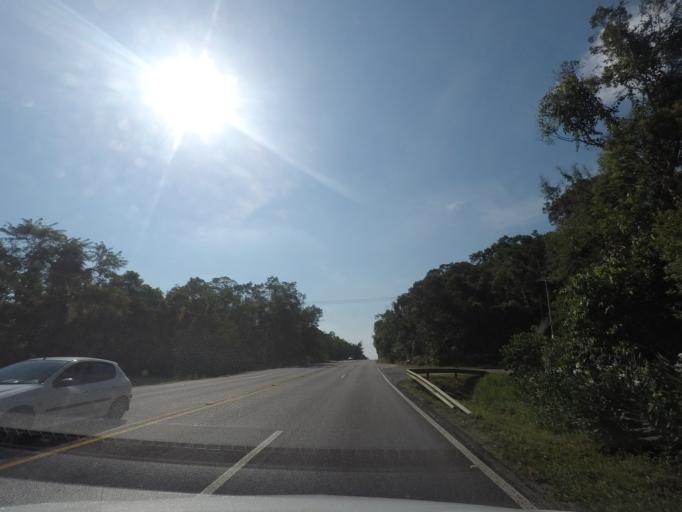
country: BR
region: Parana
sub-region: Paranagua
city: Paranagua
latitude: -25.5976
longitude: -48.6104
